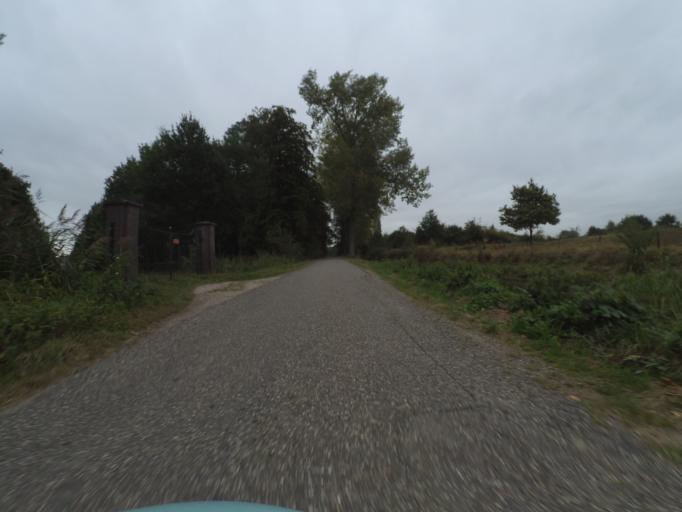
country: NL
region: Gelderland
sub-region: Gemeente Tiel
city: Tiel
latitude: 51.9063
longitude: 5.3928
